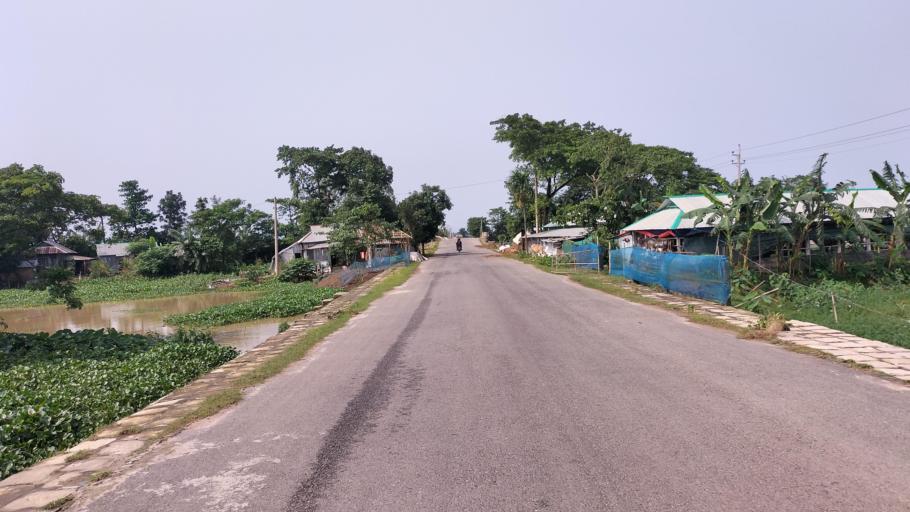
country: BD
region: Dhaka
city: Netrakona
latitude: 25.0154
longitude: 90.8550
